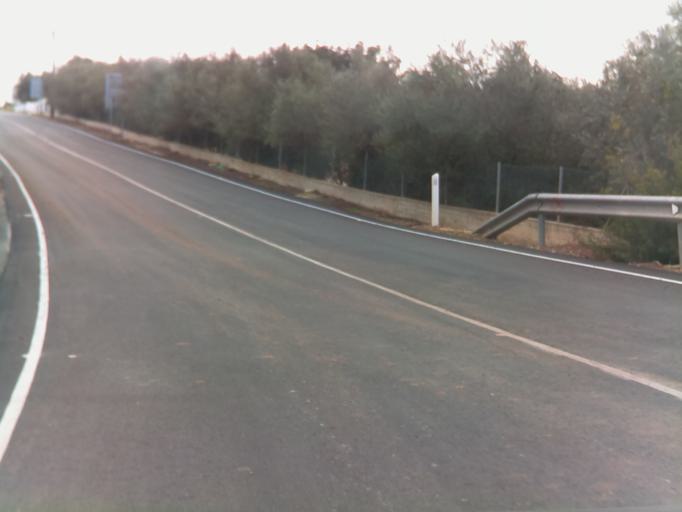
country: CY
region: Pafos
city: Polis
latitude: 35.0457
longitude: 32.3582
